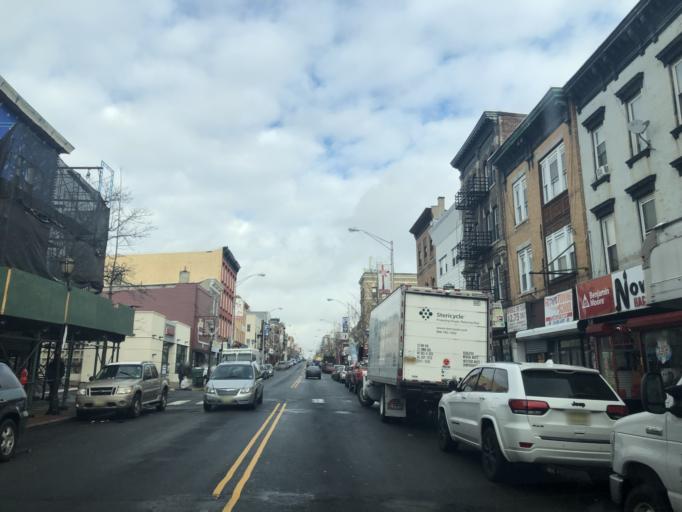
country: US
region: New Jersey
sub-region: Hudson County
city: Hoboken
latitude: 40.7451
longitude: -74.0501
